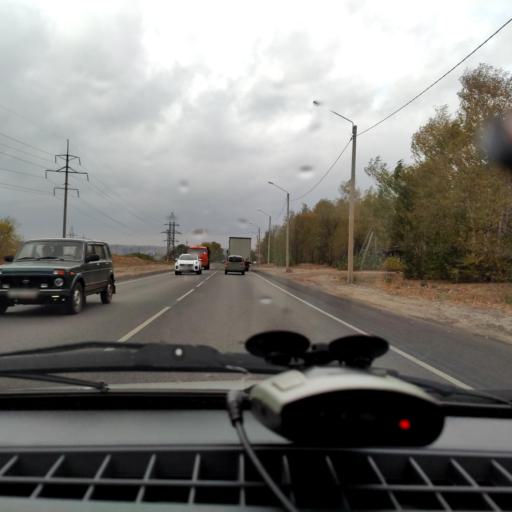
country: RU
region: Voronezj
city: Pridonskoy
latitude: 51.6979
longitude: 39.0829
